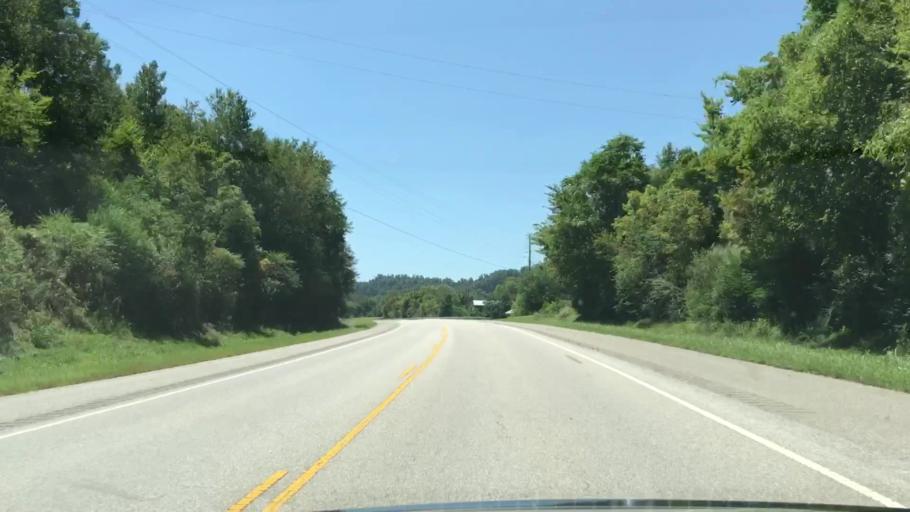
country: US
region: Tennessee
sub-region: Jackson County
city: Gainesboro
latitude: 36.4270
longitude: -85.6381
